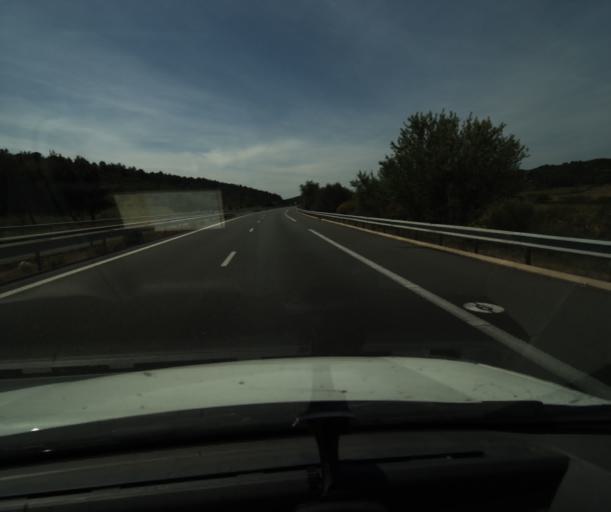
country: FR
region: Languedoc-Roussillon
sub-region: Departement de l'Aude
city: Puicheric
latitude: 43.1737
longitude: 2.6540
